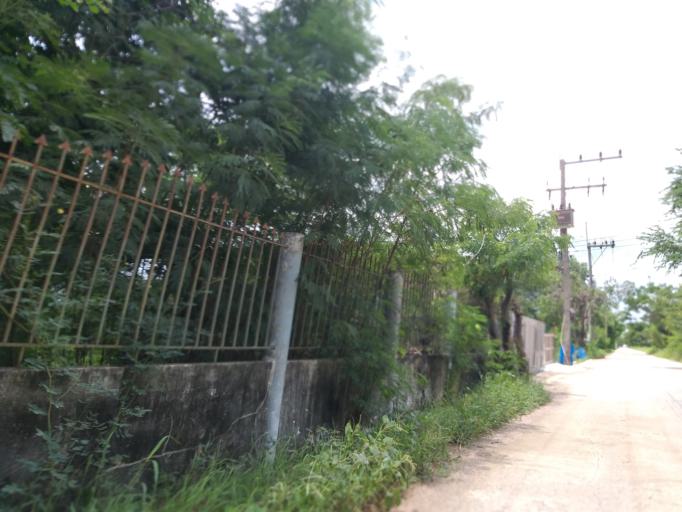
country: TH
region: Pathum Thani
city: Ban Lam Luk Ka
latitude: 13.9900
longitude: 100.8568
